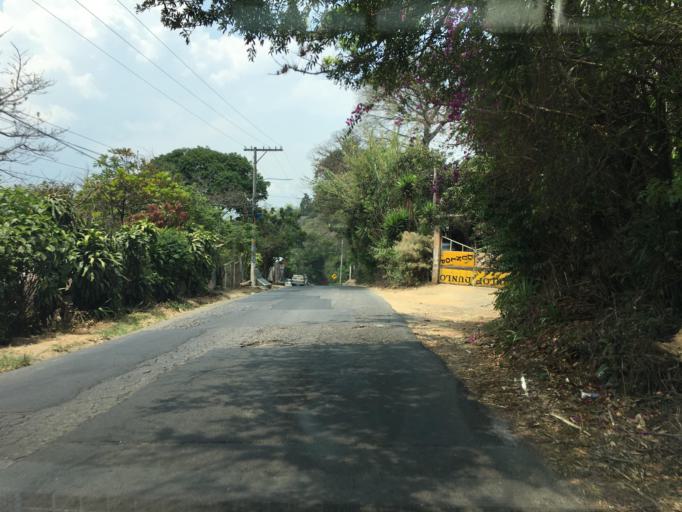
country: GT
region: Guatemala
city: Villa Canales
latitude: 14.3909
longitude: -90.5496
